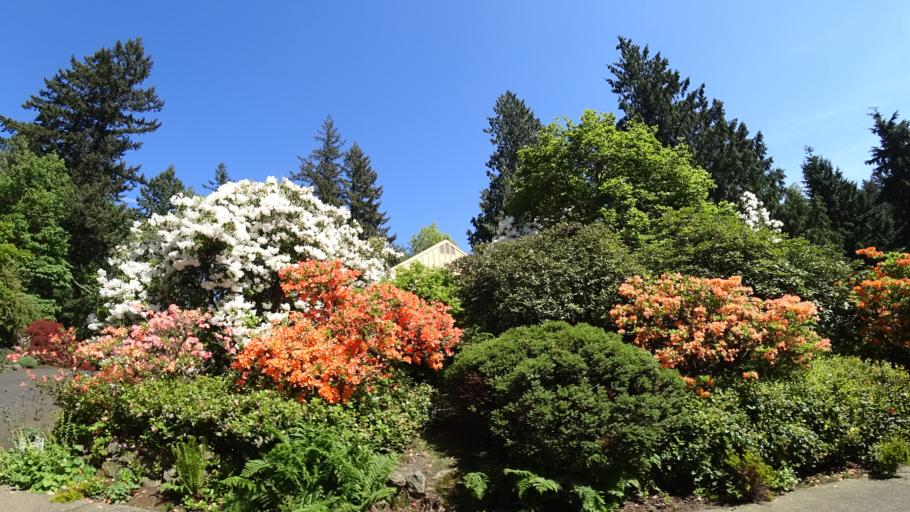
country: US
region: Oregon
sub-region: Washington County
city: Raleigh Hills
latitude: 45.4918
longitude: -122.7394
